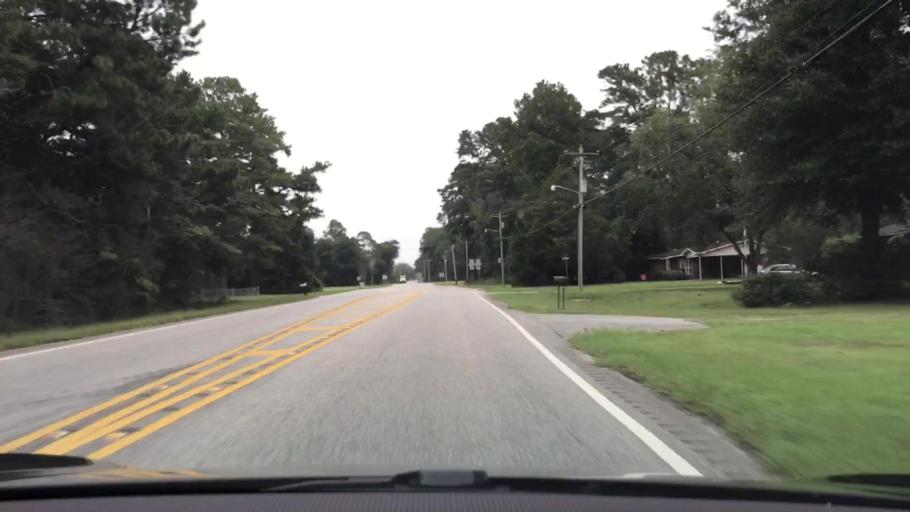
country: US
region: Alabama
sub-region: Coffee County
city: Elba
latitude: 31.4033
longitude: -86.0825
